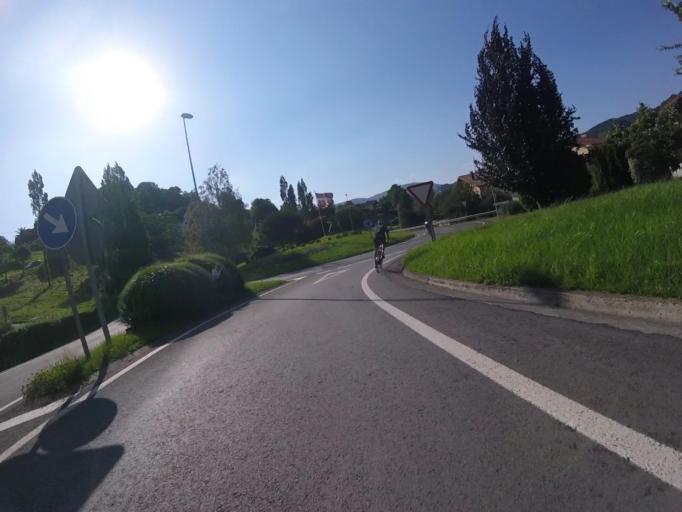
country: ES
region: Basque Country
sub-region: Provincia de Guipuzcoa
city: Asteasu
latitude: 43.1937
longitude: -2.0949
